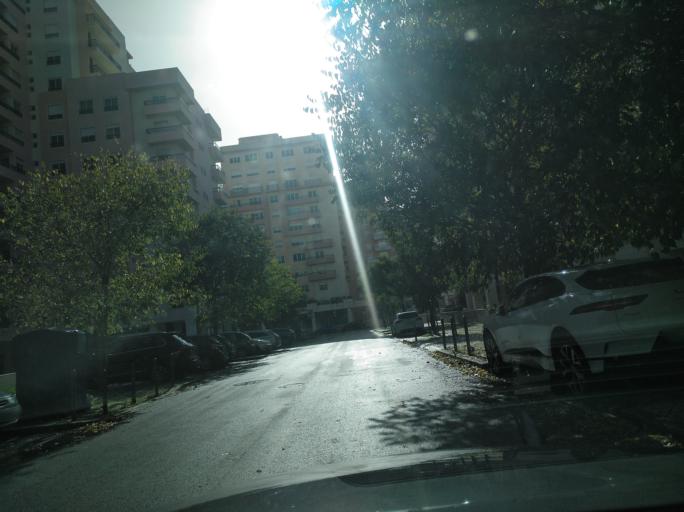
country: PT
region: Lisbon
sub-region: Odivelas
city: Pontinha
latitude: 38.7629
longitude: -9.1746
